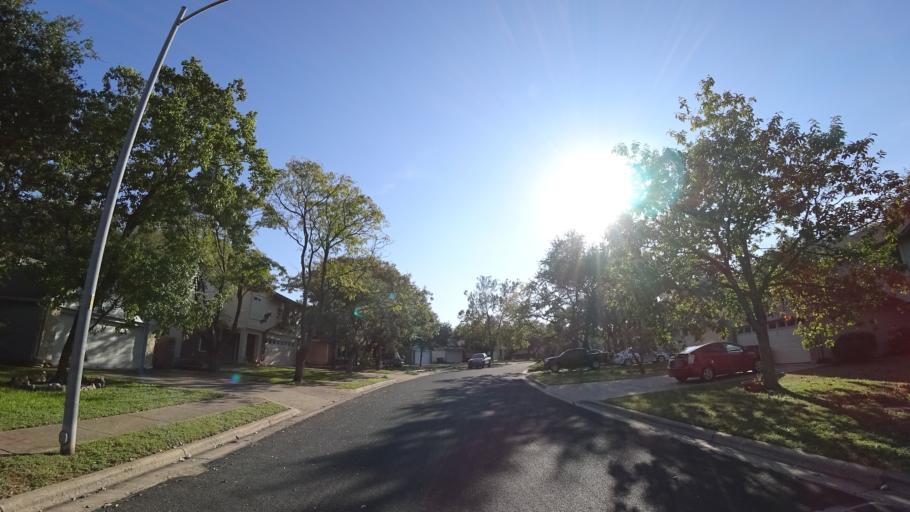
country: US
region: Texas
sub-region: Travis County
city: Shady Hollow
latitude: 30.2057
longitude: -97.8458
